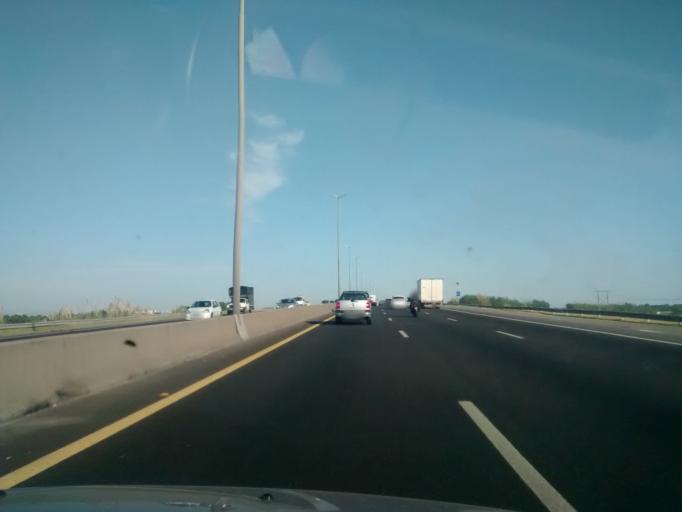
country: AR
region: Buenos Aires
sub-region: Partido de Quilmes
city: Quilmes
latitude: -34.7428
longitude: -58.2048
